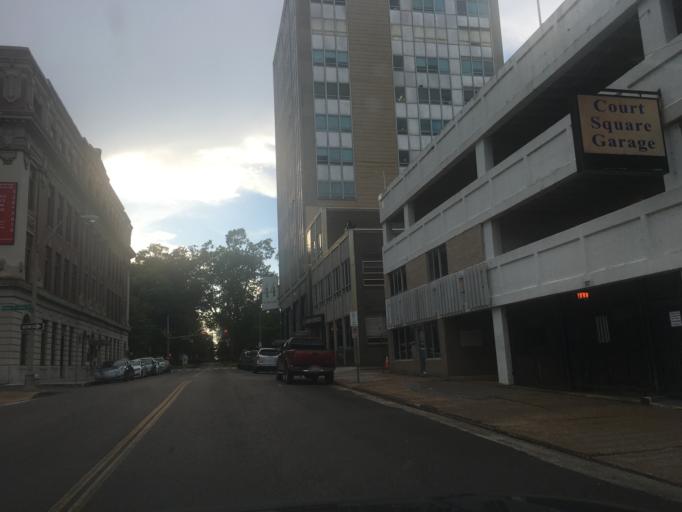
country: US
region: Tennessee
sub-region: Shelby County
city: Memphis
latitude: 35.1456
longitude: -90.0501
